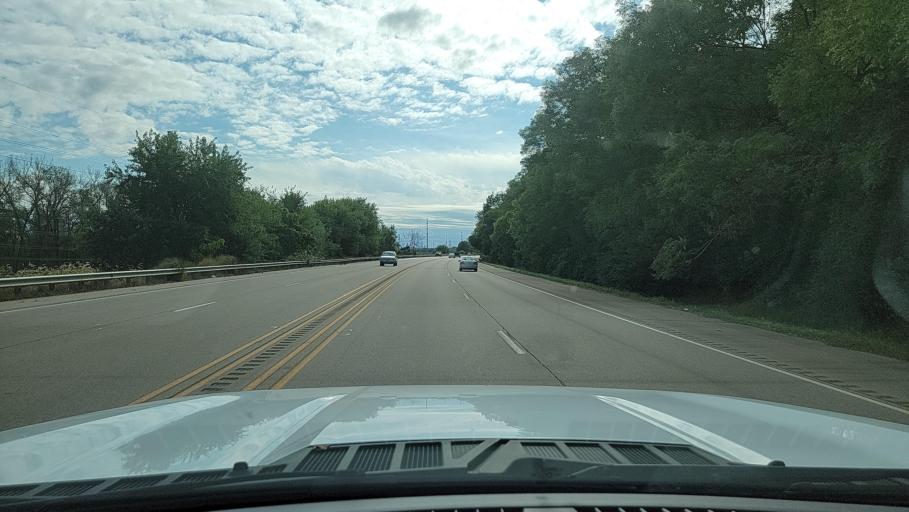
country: US
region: Illinois
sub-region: Tazewell County
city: North Pekin
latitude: 40.6109
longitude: -89.6599
